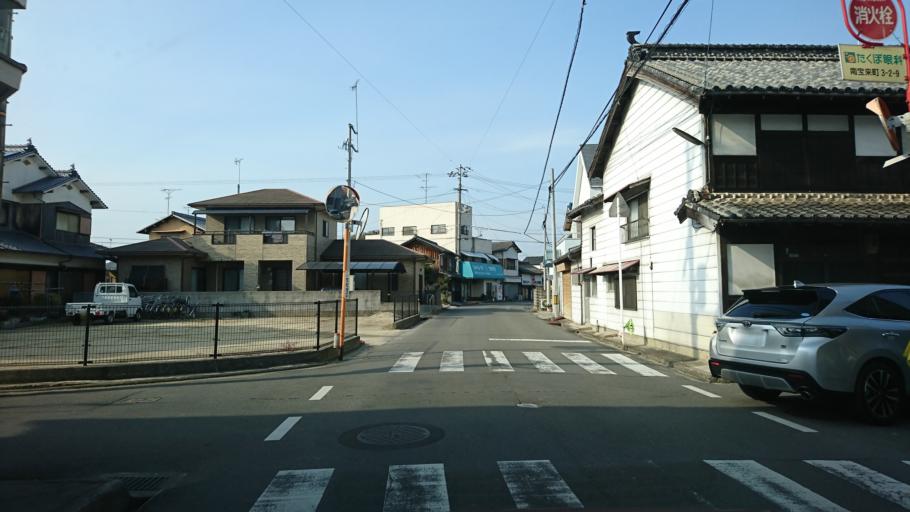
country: JP
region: Ehime
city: Saijo
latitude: 34.0213
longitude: 133.0396
